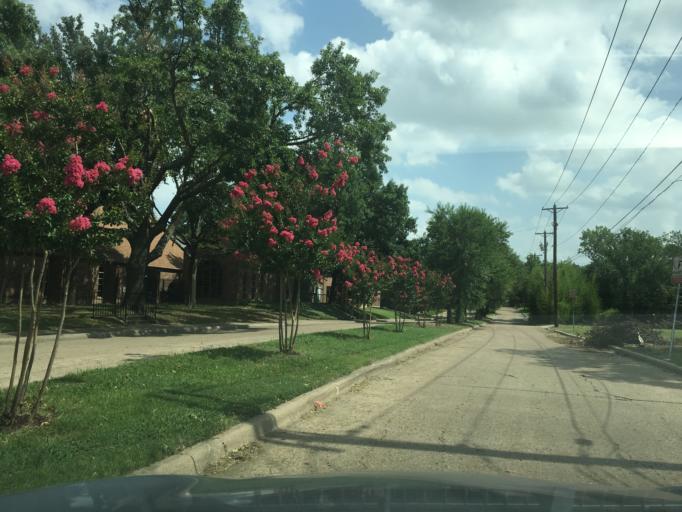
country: US
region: Texas
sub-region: Dallas County
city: University Park
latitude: 32.8948
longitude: -96.8126
